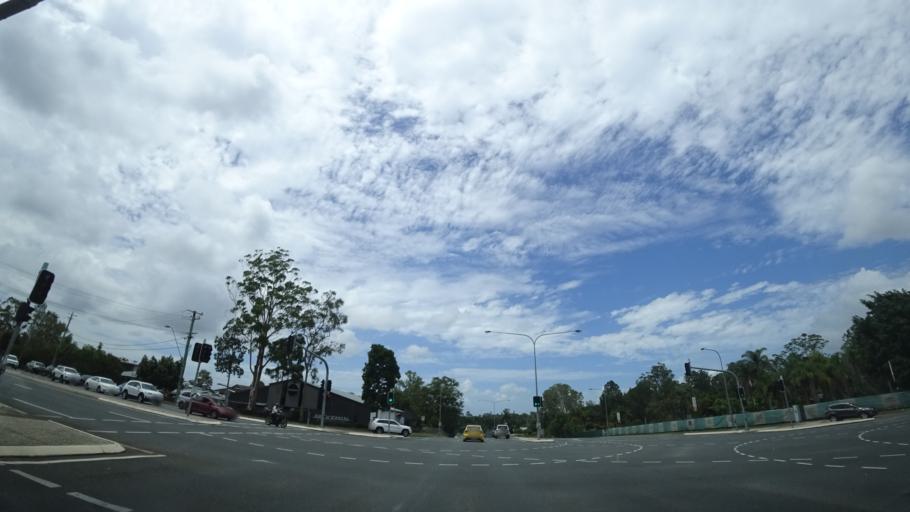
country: AU
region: Queensland
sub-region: Brisbane
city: Bridegman Downs
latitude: -27.3552
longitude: 152.9940
